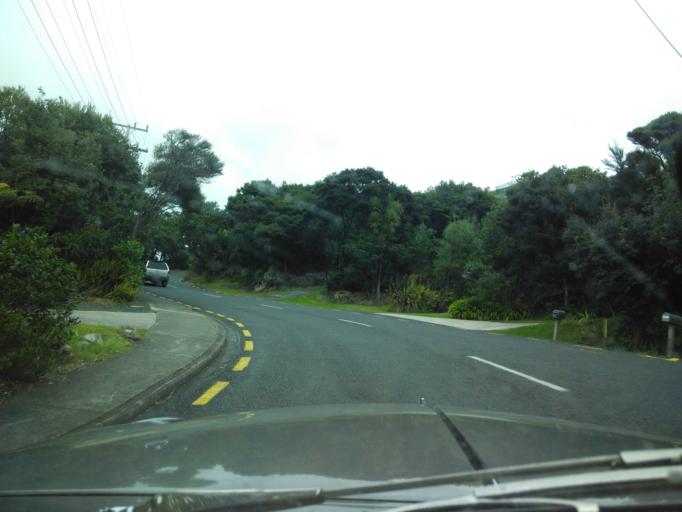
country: NZ
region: Auckland
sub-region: Auckland
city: Wellsford
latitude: -36.0823
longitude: 174.5892
